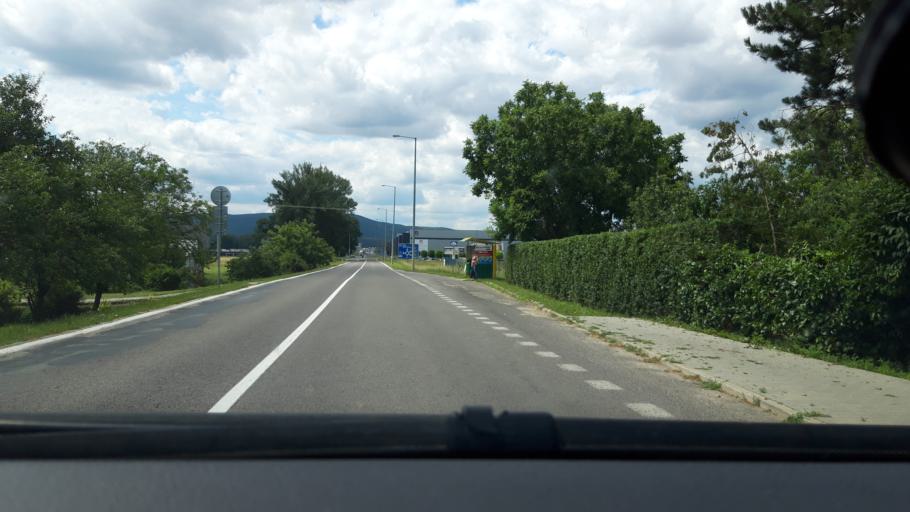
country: SK
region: Trenciansky
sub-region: Okres Nove Mesto nad Vahom
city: Nove Mesto nad Vahom
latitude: 48.7608
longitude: 17.8822
